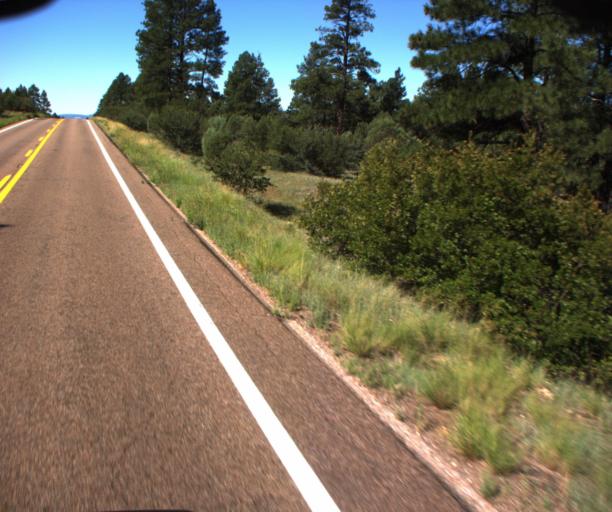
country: US
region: Arizona
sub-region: Navajo County
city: Linden
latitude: 34.0832
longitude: -110.1851
